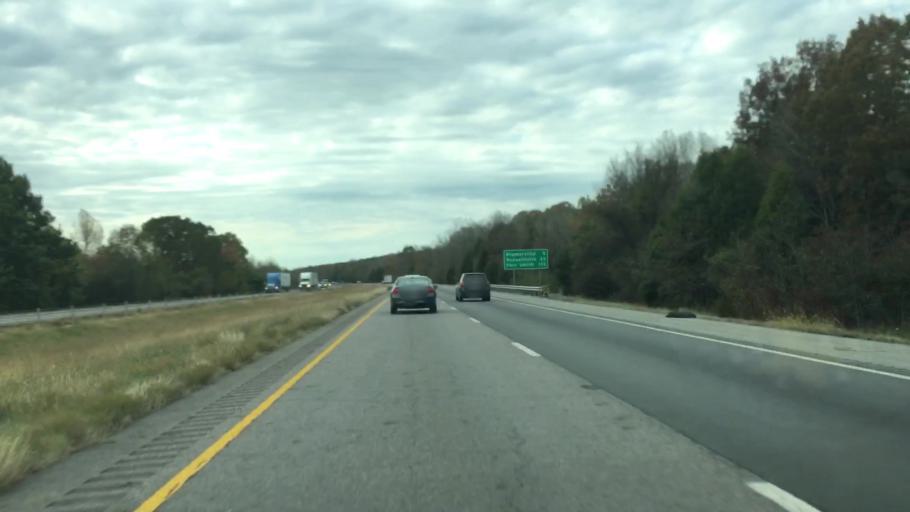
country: US
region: Arkansas
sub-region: Faulkner County
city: Conway
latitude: 35.1566
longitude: -92.5650
